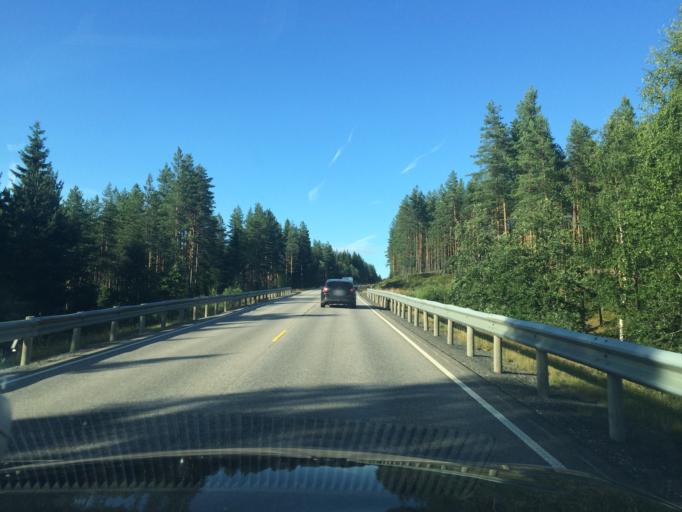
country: NO
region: Hedmark
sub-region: Elverum
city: Elverum
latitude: 60.9557
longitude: 11.7039
